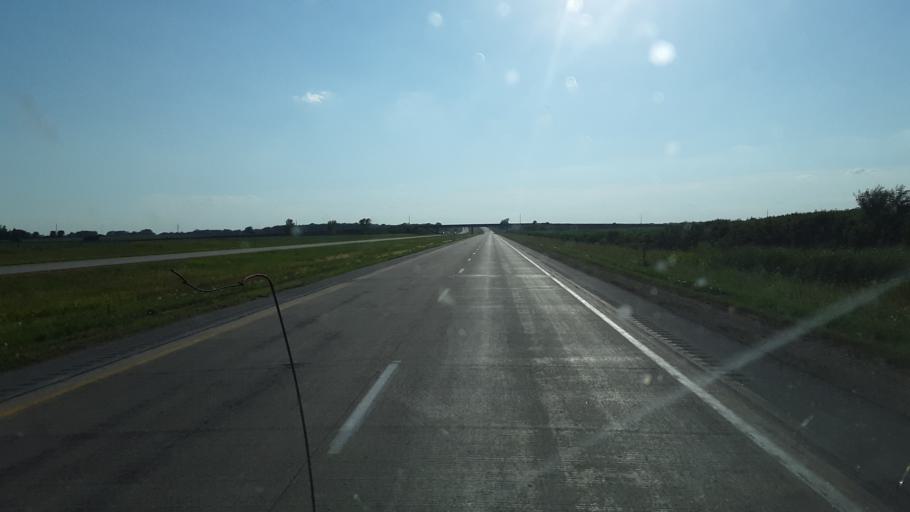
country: US
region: Iowa
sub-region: Hardin County
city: Iowa Falls
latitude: 42.4486
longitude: -93.3392
